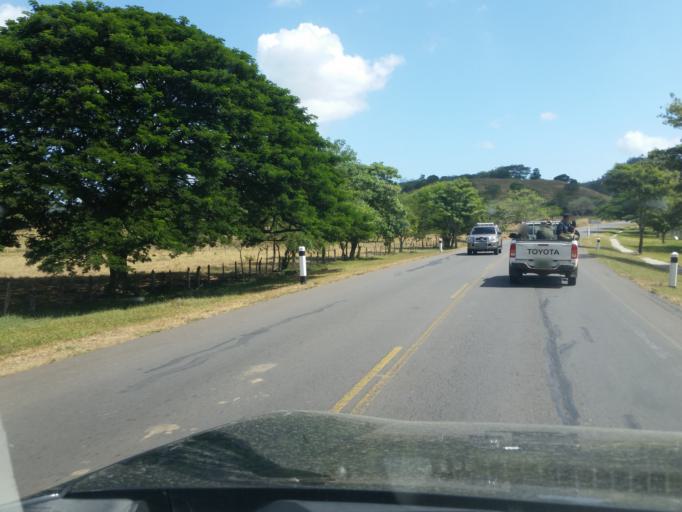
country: NI
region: Chontales
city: Comalapa
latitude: 12.1913
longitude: -85.6061
